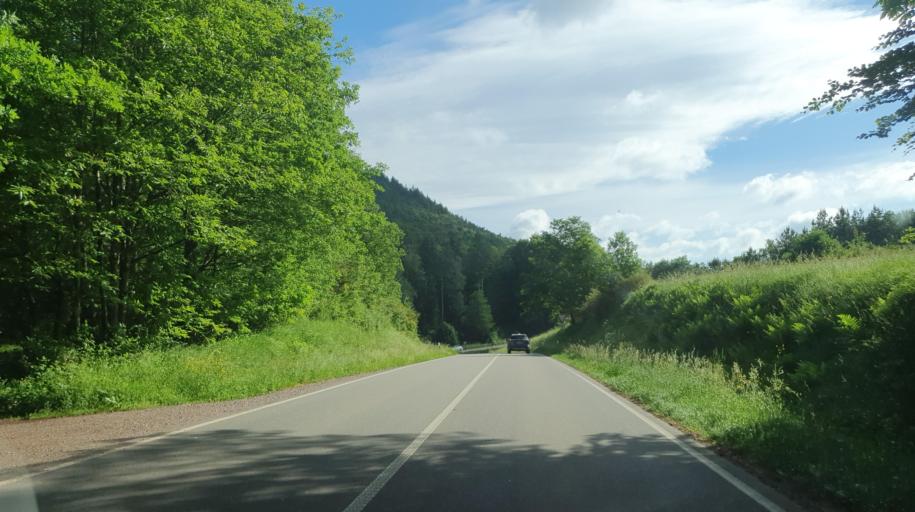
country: DE
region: Rheinland-Pfalz
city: Wernersberg
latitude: 49.1790
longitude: 7.9454
